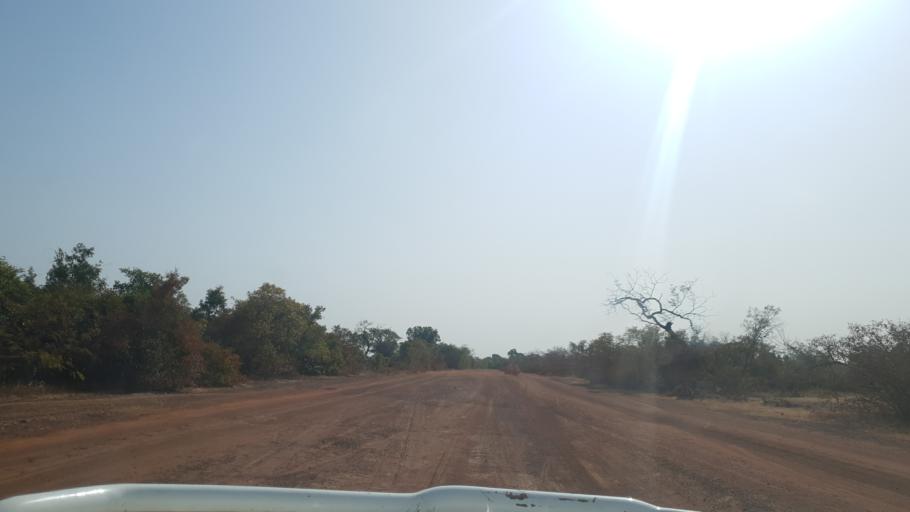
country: ML
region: Koulikoro
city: Dioila
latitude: 12.6714
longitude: -6.7055
